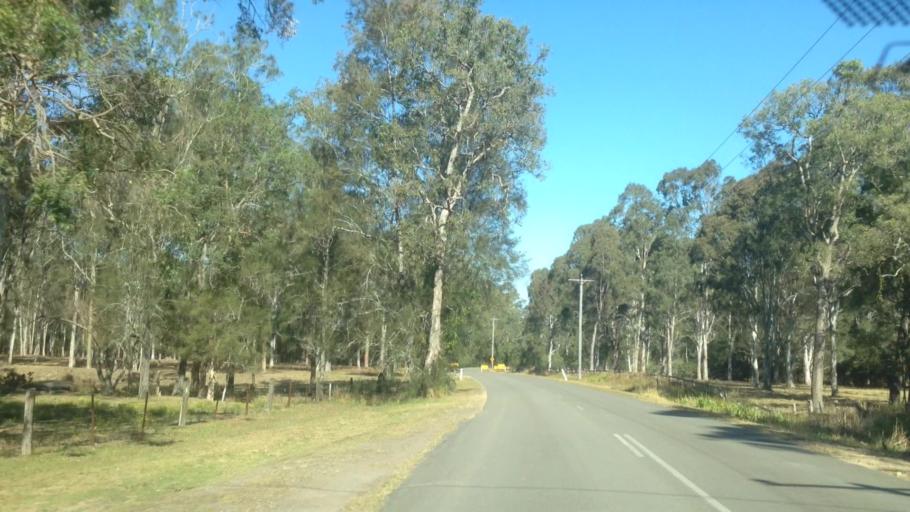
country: AU
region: New South Wales
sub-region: Lake Macquarie Shire
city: Cooranbong
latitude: -33.0946
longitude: 151.4519
